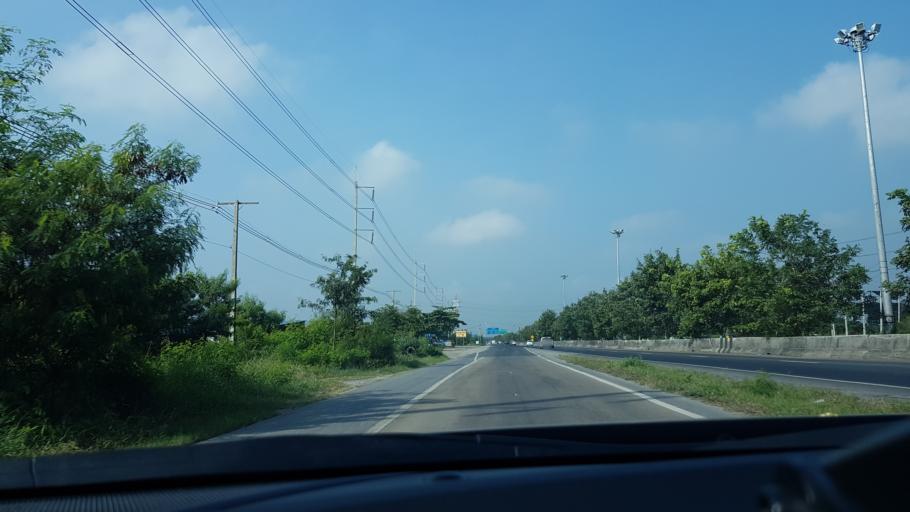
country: TH
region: Phra Nakhon Si Ayutthaya
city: Bang Pa-in
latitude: 14.1533
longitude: 100.5623
